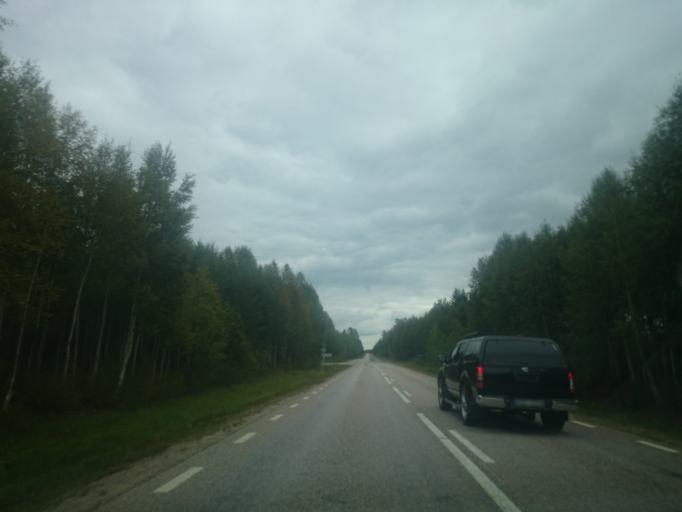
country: SE
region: Gaevleborg
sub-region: Ljusdals Kommun
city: Farila
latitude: 61.9956
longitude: 15.2425
